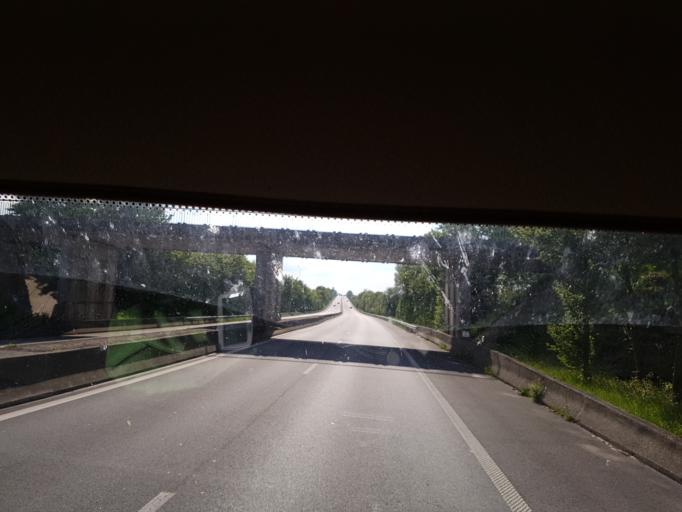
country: FR
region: Nord-Pas-de-Calais
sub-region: Departement du Pas-de-Calais
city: Saint-Pol-sur-Ternoise
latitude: 50.3685
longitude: 2.3587
